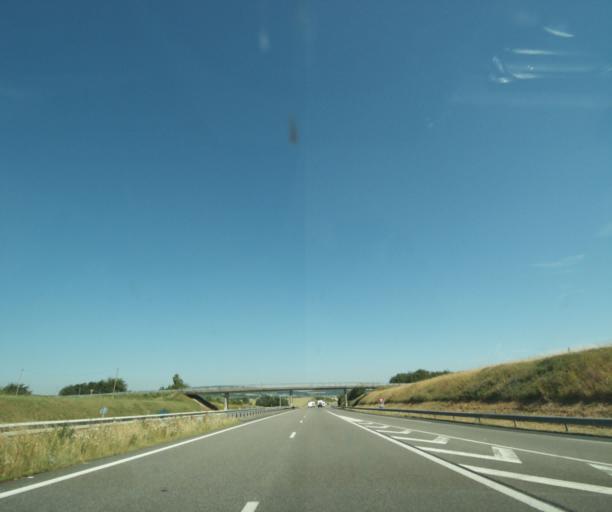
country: FR
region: Lorraine
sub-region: Departement des Vosges
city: Chatenois
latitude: 48.2712
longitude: 5.8598
